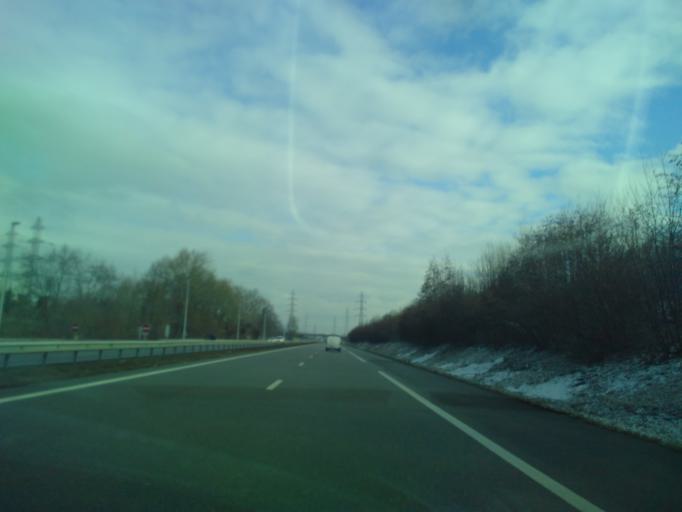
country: FR
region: Rhone-Alpes
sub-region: Departement de la Haute-Savoie
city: Seynod
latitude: 45.8768
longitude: 6.0717
